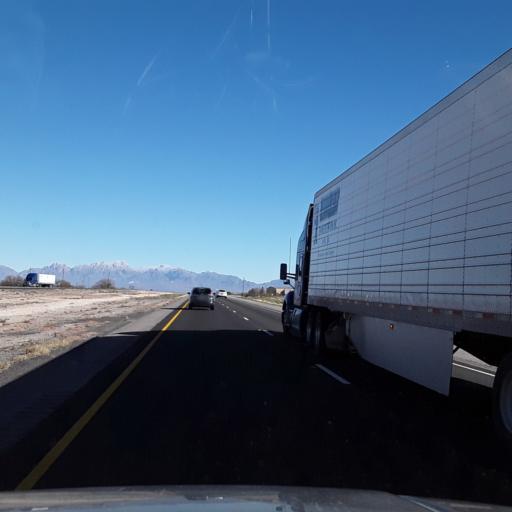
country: US
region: New Mexico
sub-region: Dona Ana County
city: Mesilla
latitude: 32.2719
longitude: -106.9210
